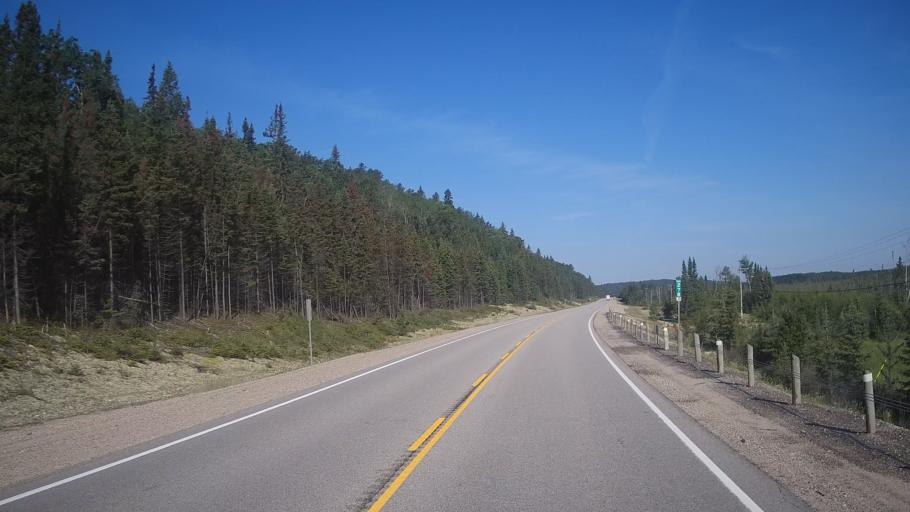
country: CA
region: Ontario
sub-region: Rainy River District
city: Atikokan
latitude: 49.4659
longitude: -91.9110
